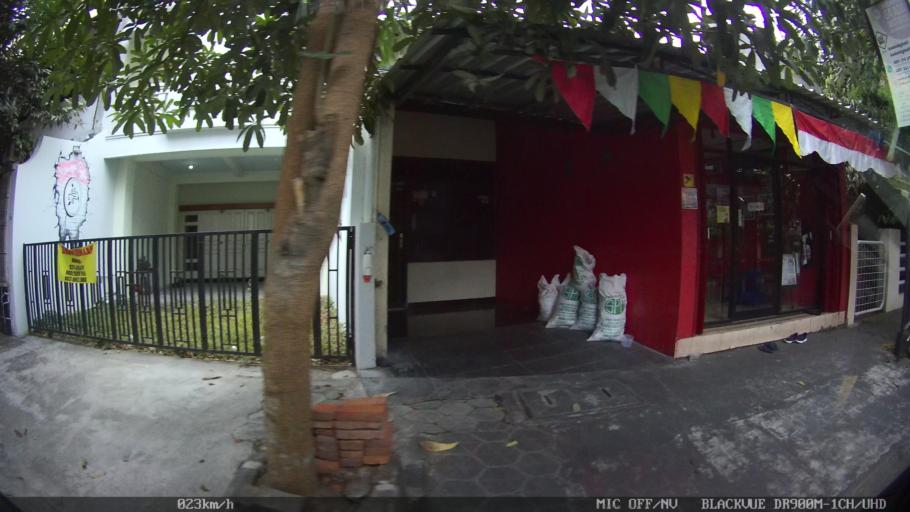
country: ID
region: Daerah Istimewa Yogyakarta
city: Yogyakarta
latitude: -7.7932
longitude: 110.3838
